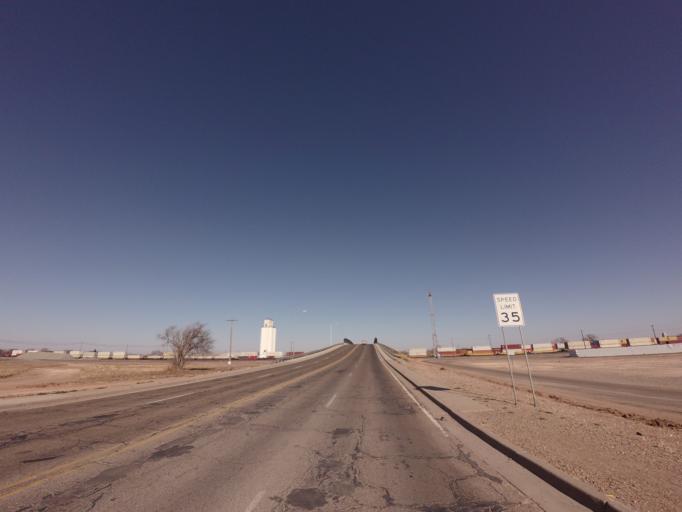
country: US
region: New Mexico
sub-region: Curry County
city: Clovis
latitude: 34.3962
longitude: -103.2204
